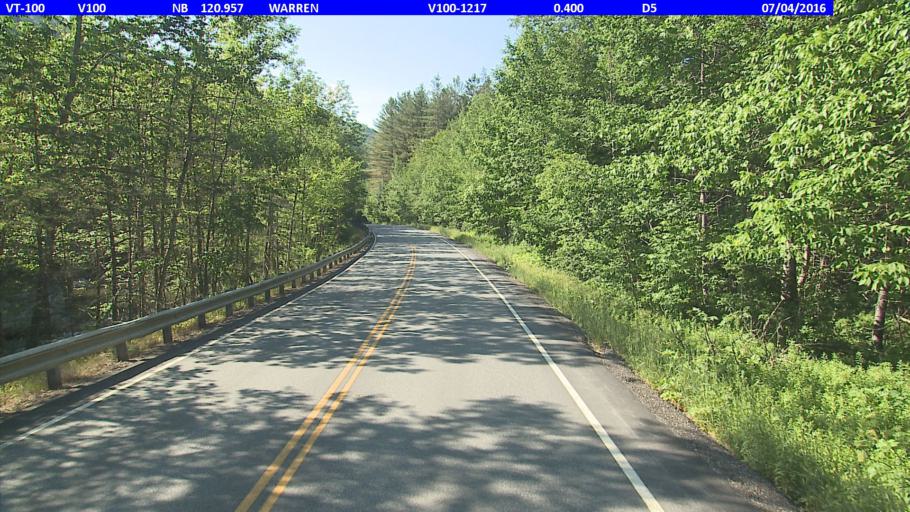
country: US
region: Vermont
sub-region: Washington County
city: Northfield
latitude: 44.0658
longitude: -72.8566
